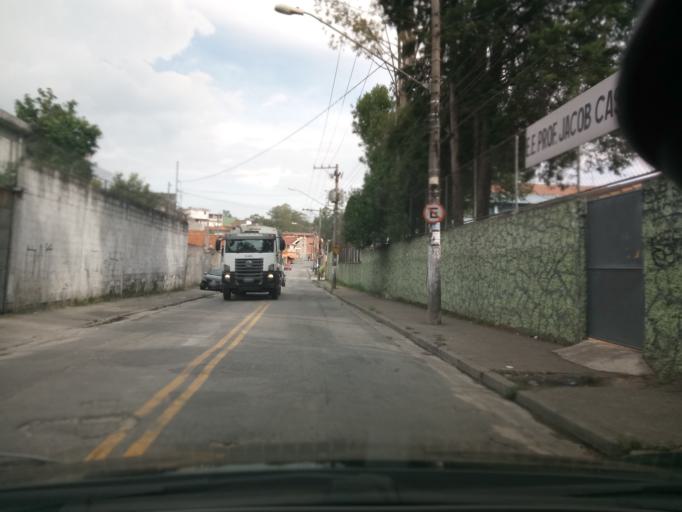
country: BR
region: Sao Paulo
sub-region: Sao Bernardo Do Campo
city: Sao Bernardo do Campo
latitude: -23.7414
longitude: -46.5960
